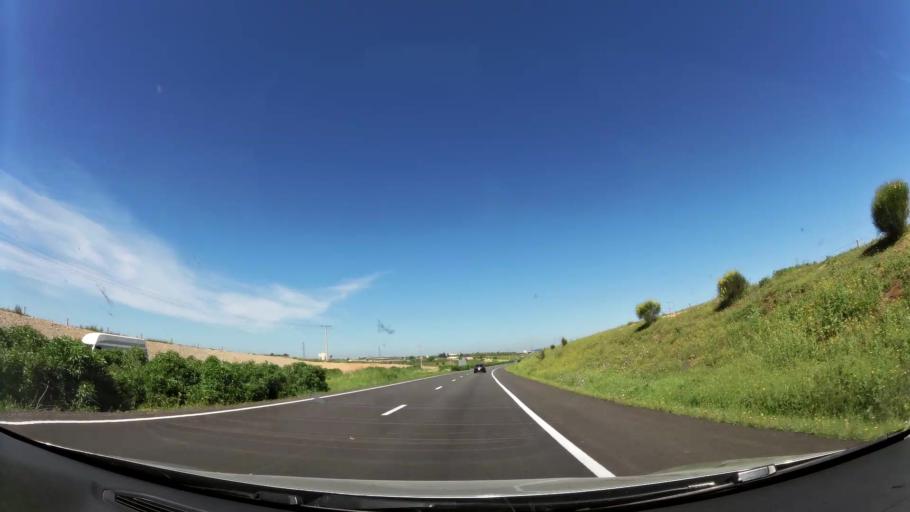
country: MA
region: Meknes-Tafilalet
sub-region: Meknes
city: Meknes
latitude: 33.8284
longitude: -5.5024
